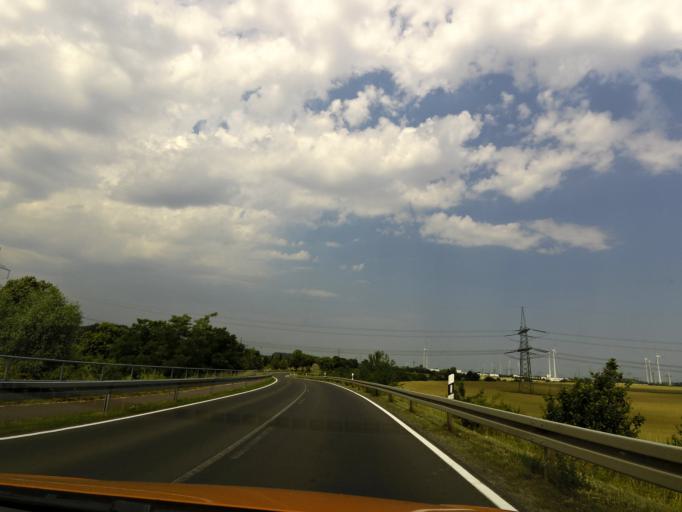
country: DE
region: Brandenburg
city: Wustermark
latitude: 52.5534
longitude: 12.9352
